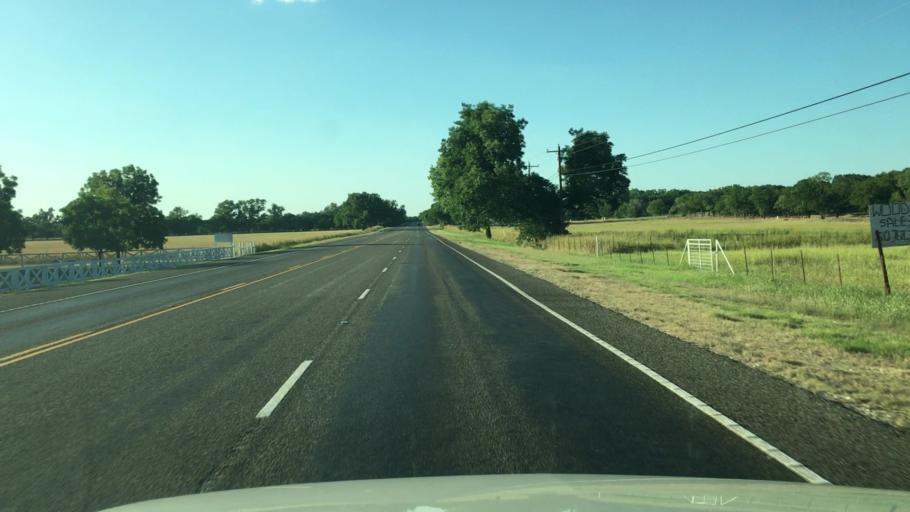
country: US
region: Texas
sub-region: Lampasas County
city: Lampasas
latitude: 31.3211
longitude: -98.1719
